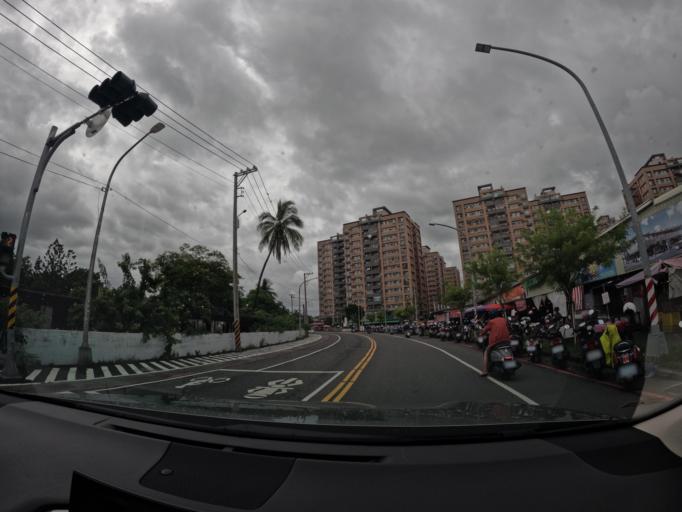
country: TW
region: Taiwan
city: Fengshan
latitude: 22.6309
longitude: 120.3729
